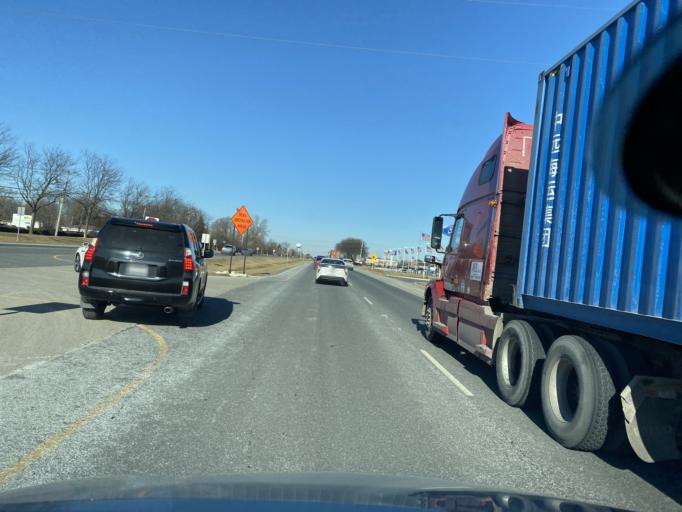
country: US
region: Illinois
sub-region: DuPage County
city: Willowbrook
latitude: 41.7536
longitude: -87.9446
